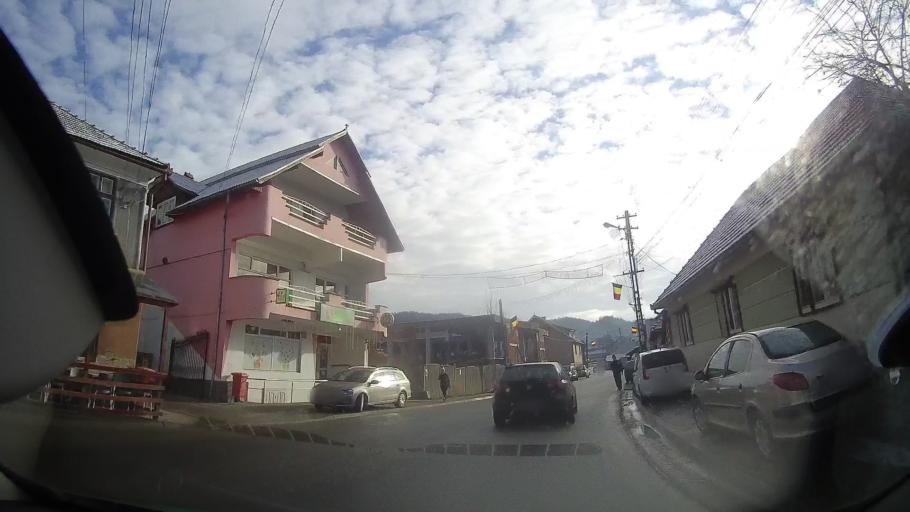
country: RO
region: Alba
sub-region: Comuna Bistra
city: Bistra
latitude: 46.3789
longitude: 23.0995
